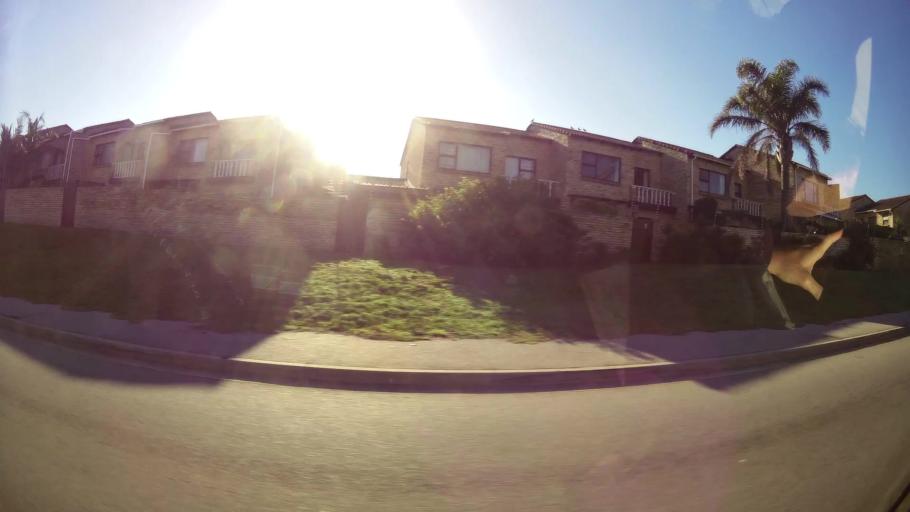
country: ZA
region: Eastern Cape
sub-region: Nelson Mandela Bay Metropolitan Municipality
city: Port Elizabeth
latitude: -33.9726
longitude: 25.6248
